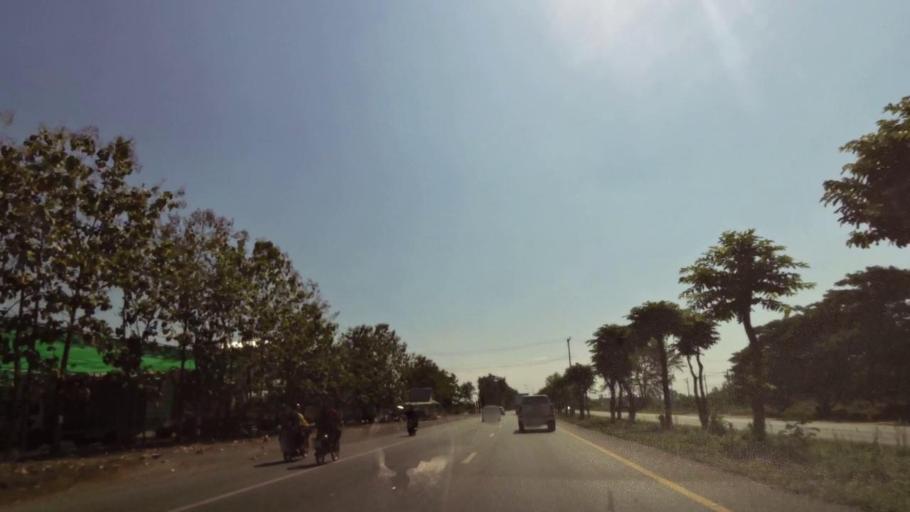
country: TH
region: Nakhon Sawan
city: Kao Liao
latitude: 15.8030
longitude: 100.1202
